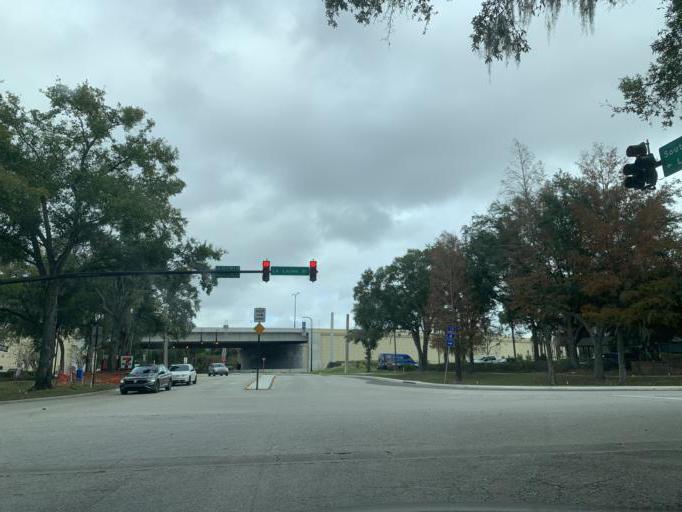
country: US
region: Florida
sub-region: Orange County
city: Eatonville
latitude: 28.6296
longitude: -81.3931
